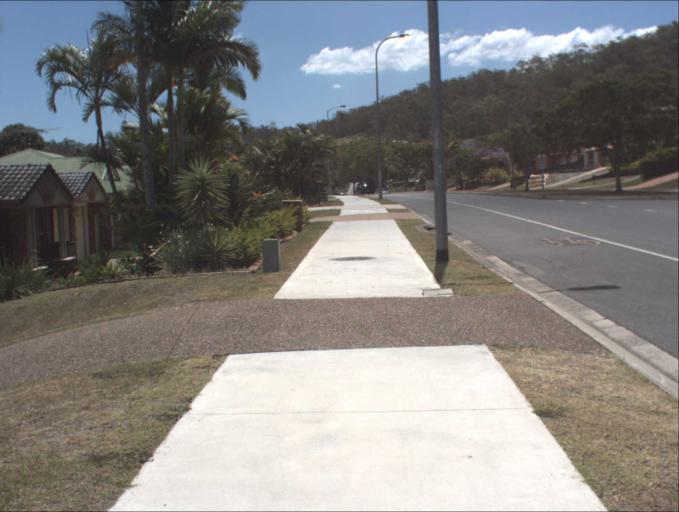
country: AU
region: Queensland
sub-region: Logan
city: Windaroo
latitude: -27.7337
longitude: 153.1992
